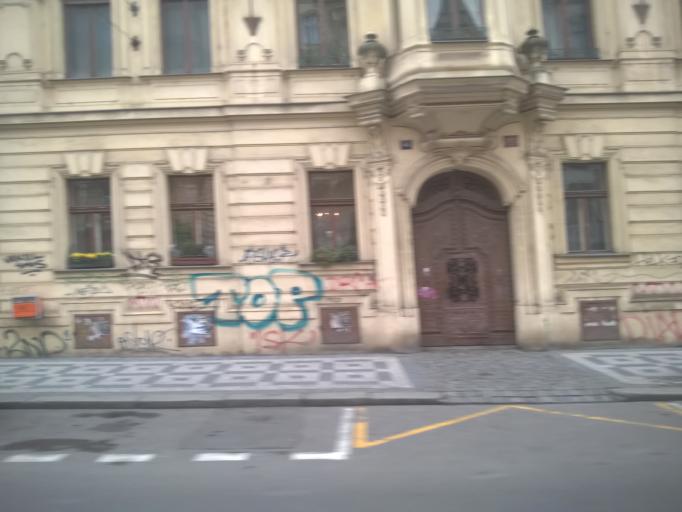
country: CZ
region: Praha
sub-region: Praha 8
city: Karlin
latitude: 50.1002
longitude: 14.4334
